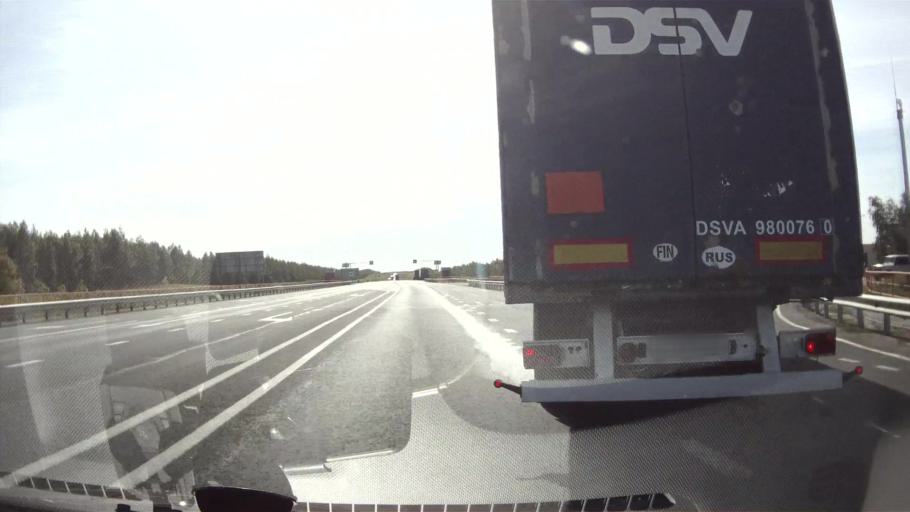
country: RU
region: Samara
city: Syzran'
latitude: 52.9244
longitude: 48.3036
